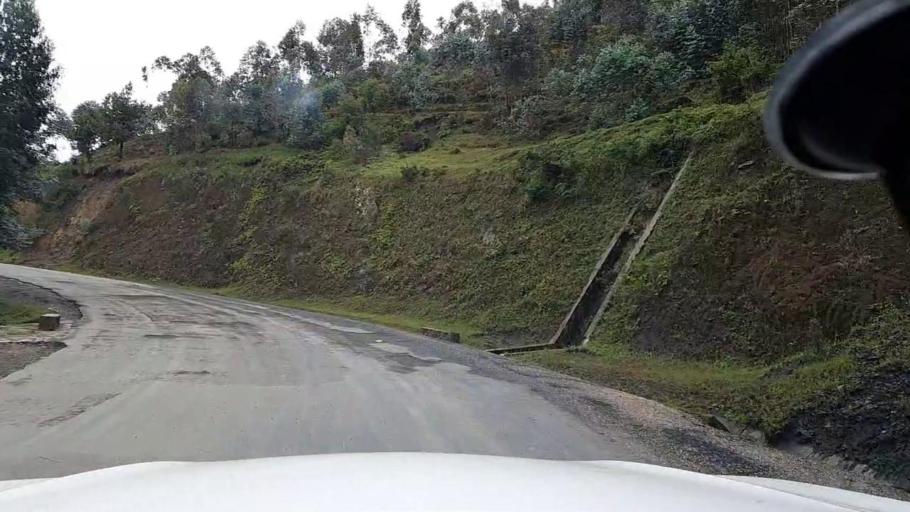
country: RW
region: Western Province
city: Kibuye
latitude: -2.0631
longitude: 29.5308
